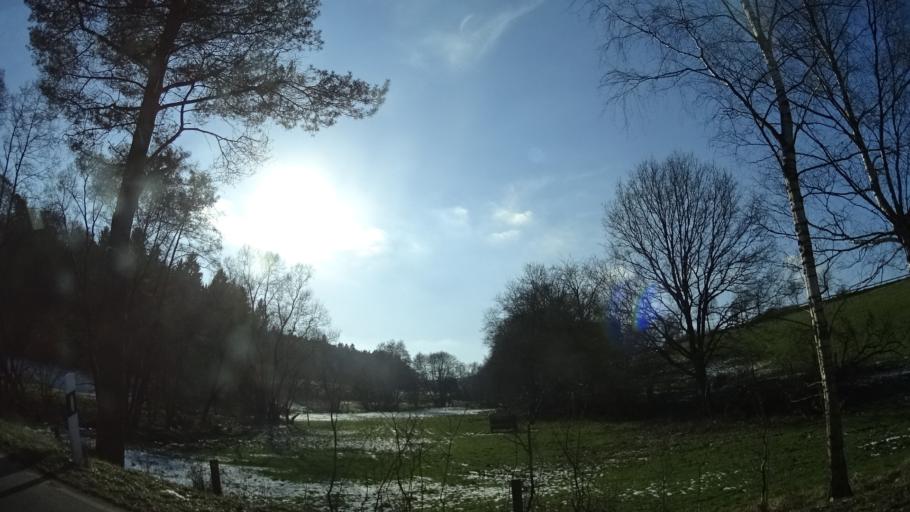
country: DE
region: Bavaria
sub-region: Regierungsbezirk Unterfranken
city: Motten
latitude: 50.4344
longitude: 9.7350
